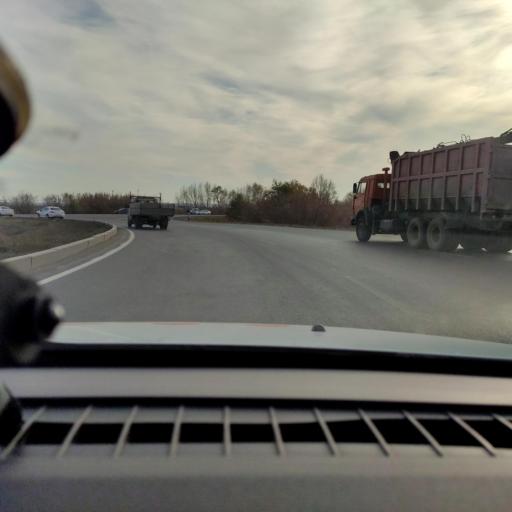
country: RU
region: Samara
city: Samara
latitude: 53.0921
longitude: 50.1500
